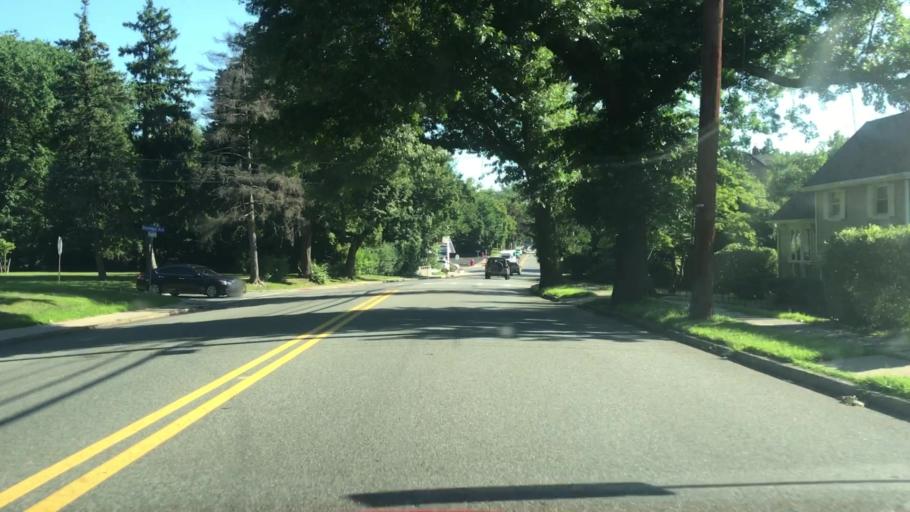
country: US
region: New Jersey
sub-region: Bergen County
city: Ridgefield Park
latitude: 40.8691
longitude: -74.0145
